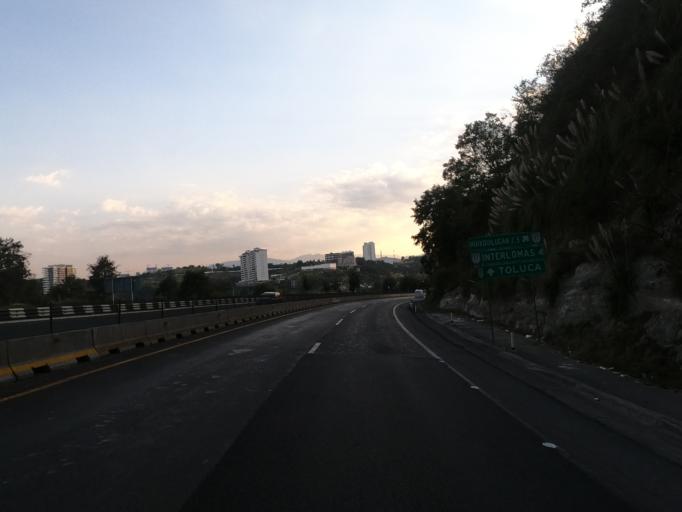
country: MX
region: Mexico
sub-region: Naucalpan de Juarez
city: Ejido el Castillo
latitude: 19.4259
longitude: -99.2952
